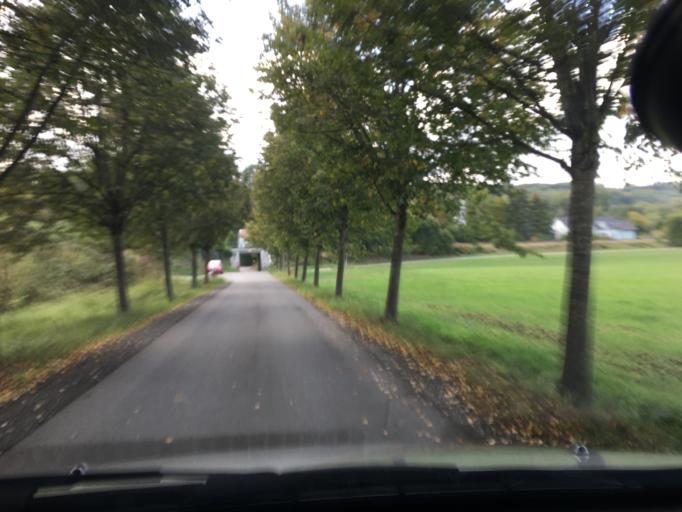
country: DE
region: Baden-Wuerttemberg
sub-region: Tuebingen Region
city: Aulendorf
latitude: 47.9604
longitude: 9.6483
